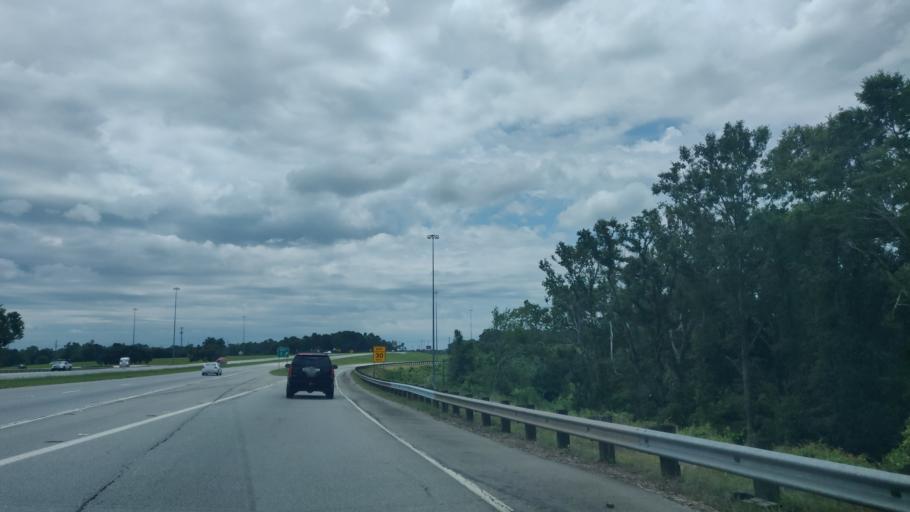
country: US
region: Georgia
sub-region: Dougherty County
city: Albany
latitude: 31.5851
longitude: -84.1132
